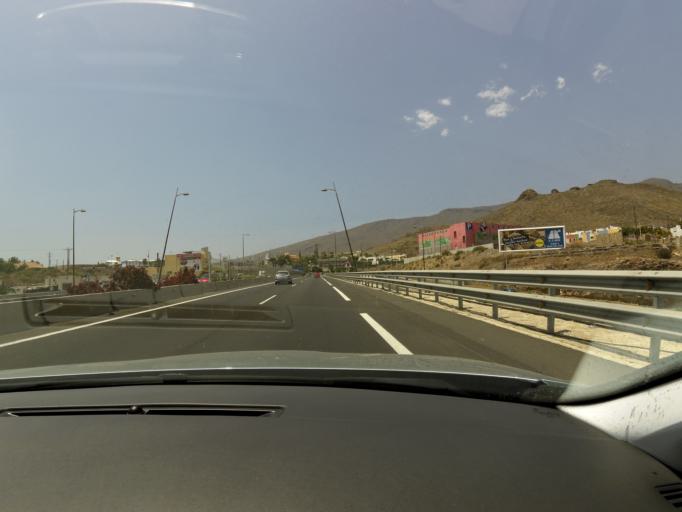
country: ES
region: Canary Islands
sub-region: Provincia de Santa Cruz de Tenerife
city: Adeje
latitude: 28.1037
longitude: -16.7313
